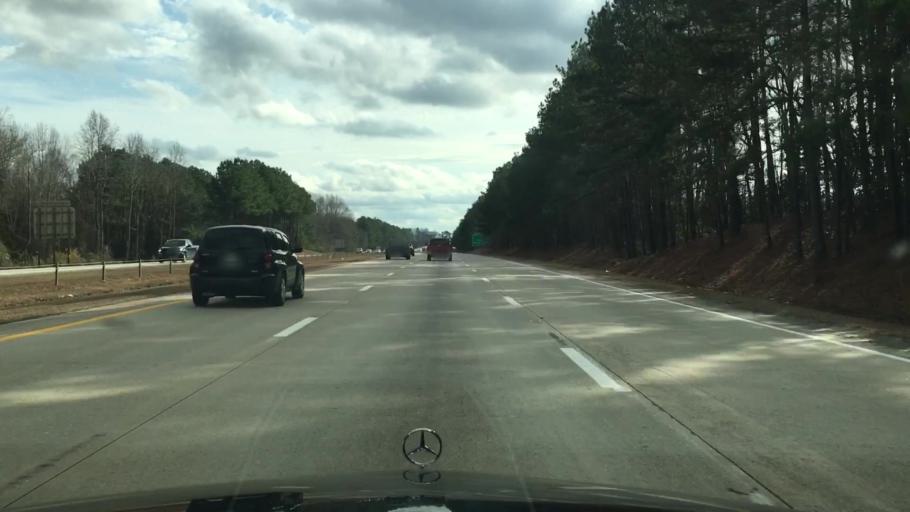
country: US
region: North Carolina
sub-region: Johnston County
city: Benson
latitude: 35.4198
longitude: -78.5288
